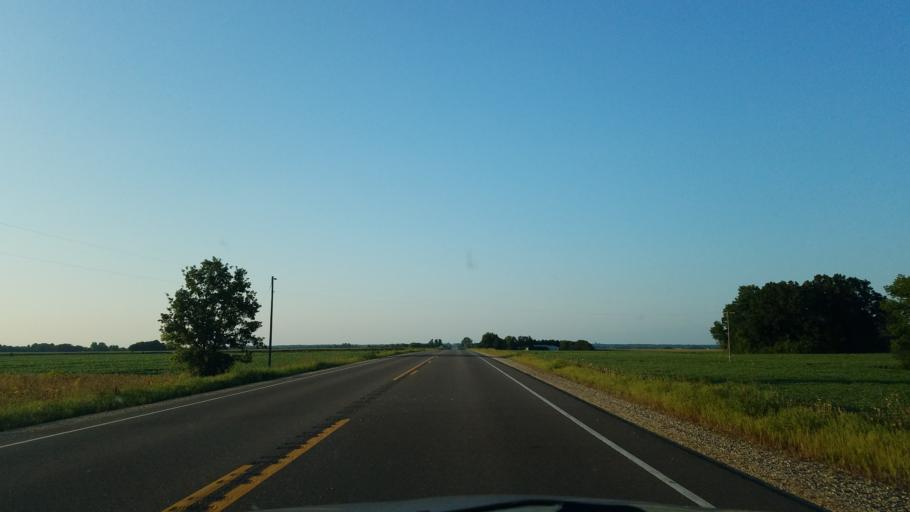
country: US
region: Wisconsin
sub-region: Polk County
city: Clear Lake
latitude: 45.2049
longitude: -92.2838
